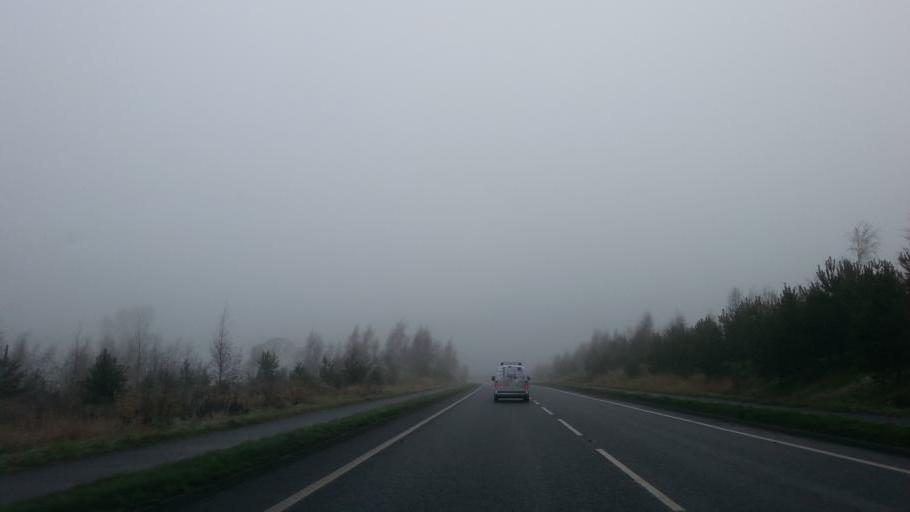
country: GB
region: England
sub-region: Cheshire East
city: Alderley Edge
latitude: 53.2810
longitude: -2.2457
